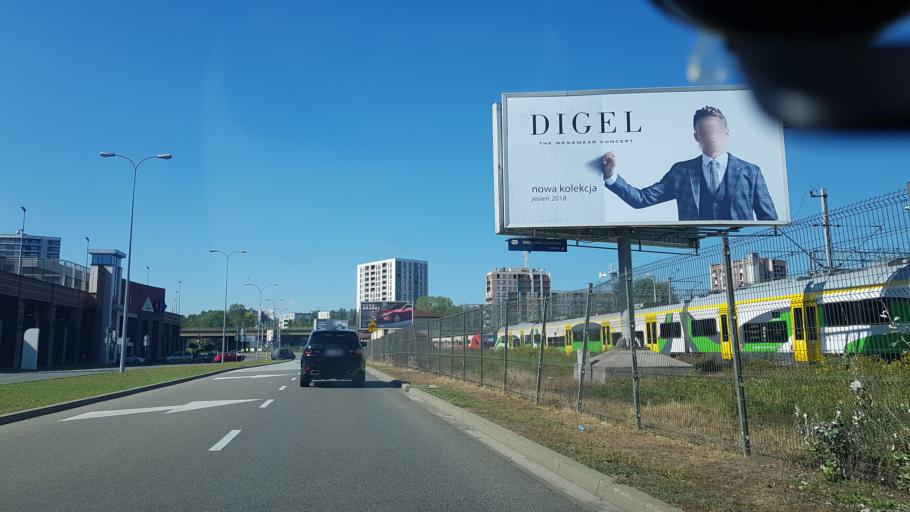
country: PL
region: Masovian Voivodeship
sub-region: Warszawa
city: Zoliborz
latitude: 52.2590
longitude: 20.9857
